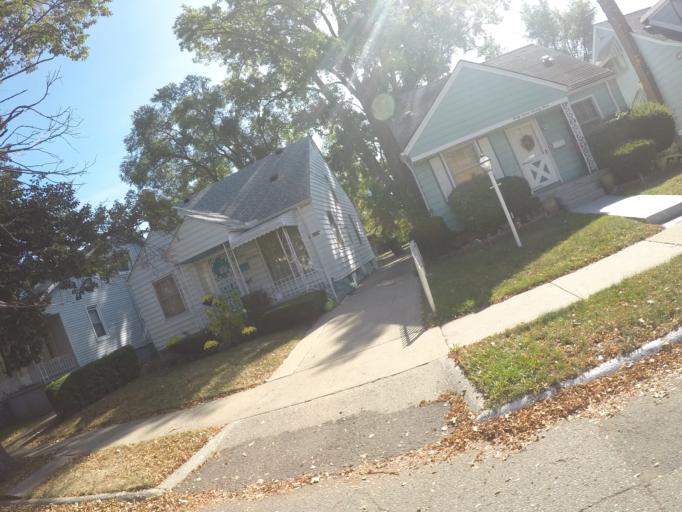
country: US
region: Michigan
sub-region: Wayne County
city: Lincoln Park
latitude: 42.2572
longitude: -83.1610
